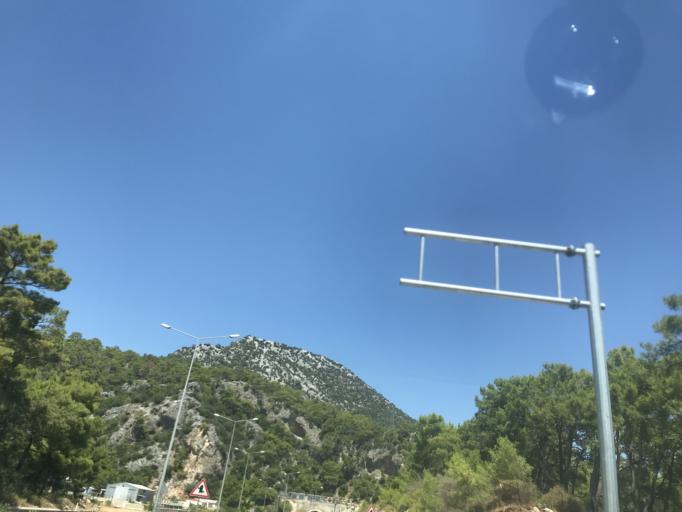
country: TR
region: Antalya
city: Cakirlar
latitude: 36.7593
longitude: 30.5698
